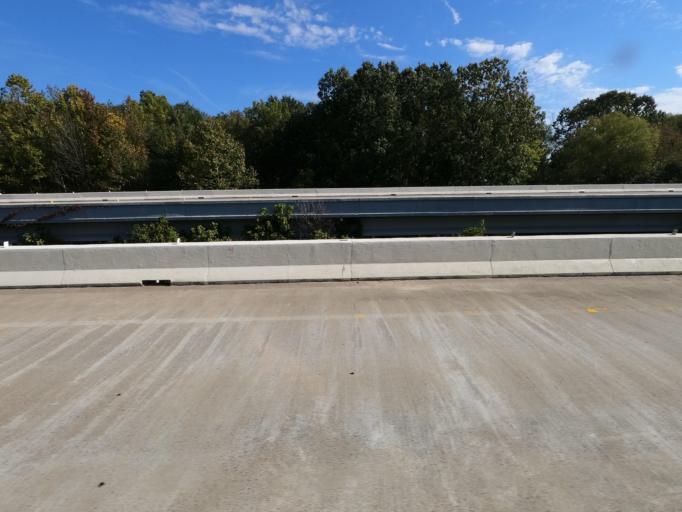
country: US
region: Tennessee
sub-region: Shelby County
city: Arlington
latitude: 35.2931
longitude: -89.6909
